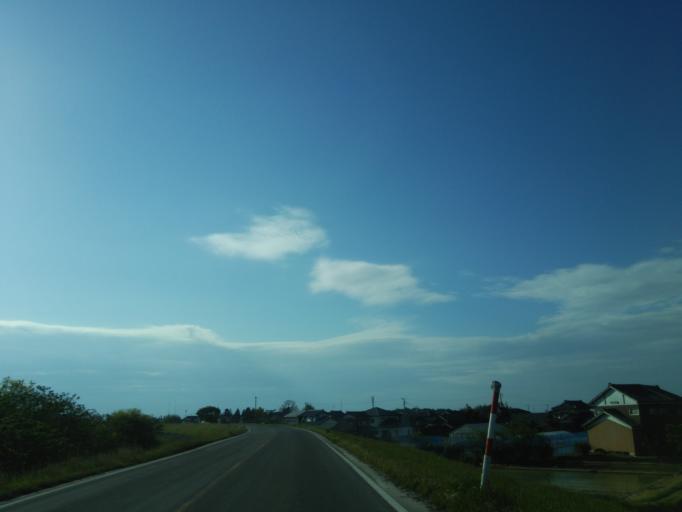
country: JP
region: Niigata
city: Niitsu-honcho
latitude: 37.8042
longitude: 139.1817
